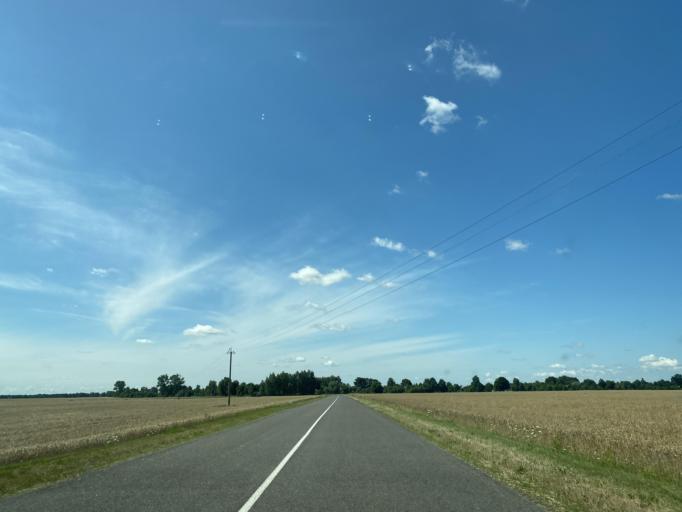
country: BY
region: Brest
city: Ivanava
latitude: 52.2068
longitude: 25.6201
